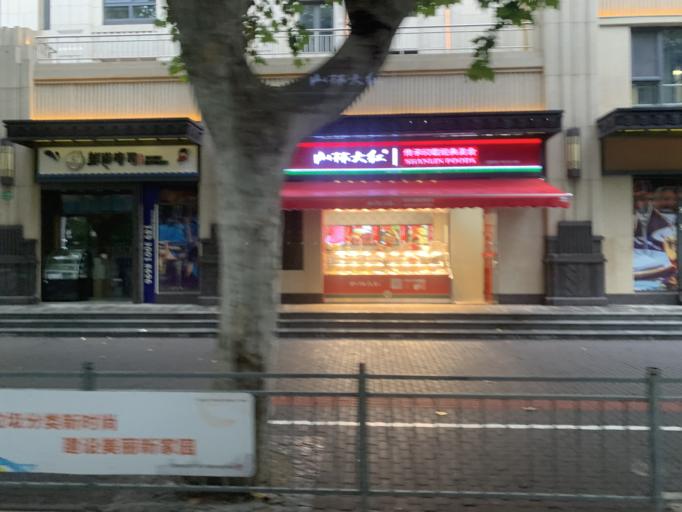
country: CN
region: Shanghai Shi
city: Luwan
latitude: 31.2135
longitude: 121.4701
